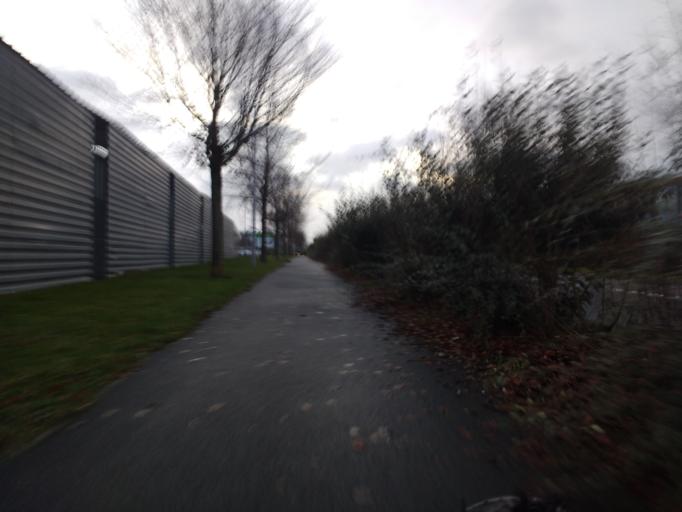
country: FR
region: Picardie
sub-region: Departement de la Somme
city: Longueau
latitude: 49.8669
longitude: 2.3668
